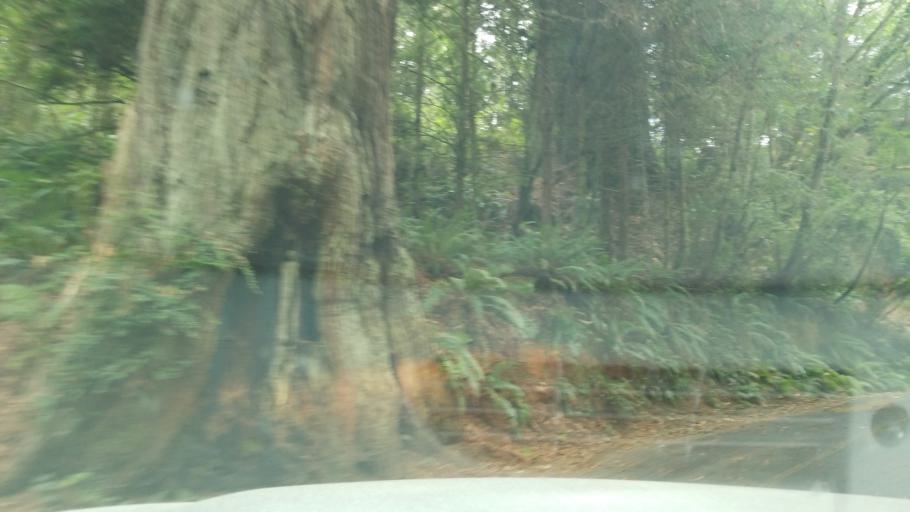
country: US
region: California
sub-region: Del Norte County
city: Bertsch-Oceanview
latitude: 41.5221
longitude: -124.0300
